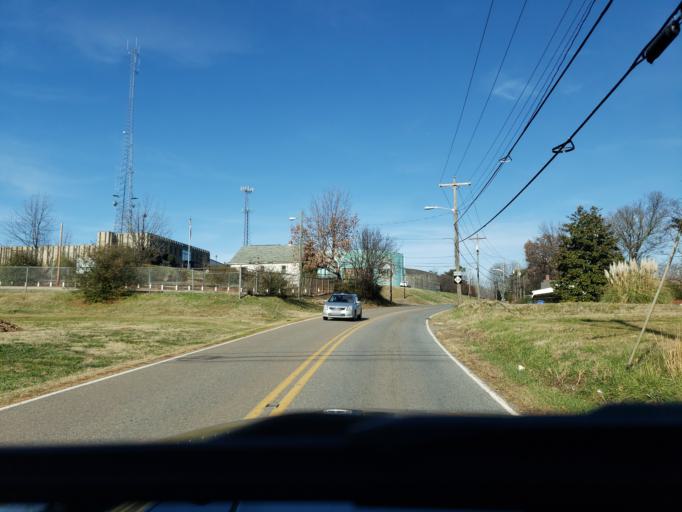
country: US
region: North Carolina
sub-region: Cleveland County
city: Kings Mountain
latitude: 35.2573
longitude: -81.3370
